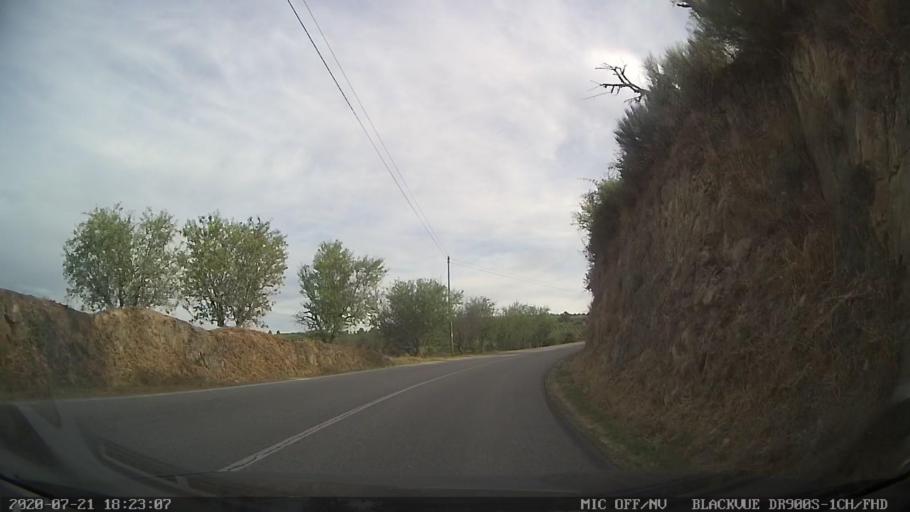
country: PT
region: Viseu
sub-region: Sao Joao da Pesqueira
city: Sao Joao da Pesqueira
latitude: 41.0788
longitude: -7.3887
